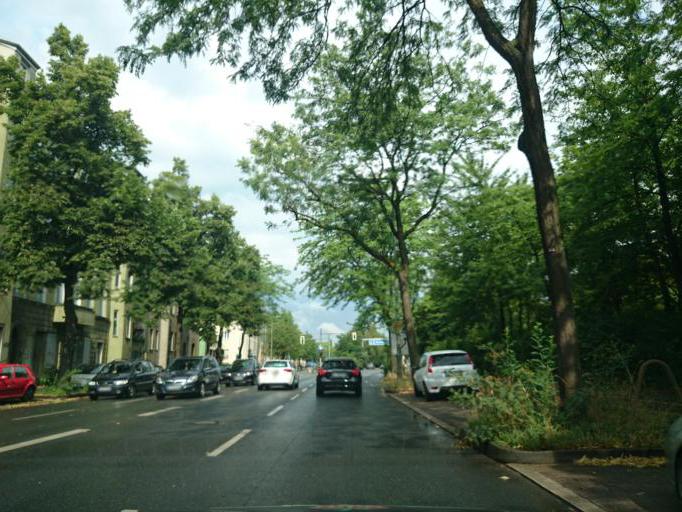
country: DE
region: Berlin
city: Friedenau
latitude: 52.4646
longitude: 13.3157
